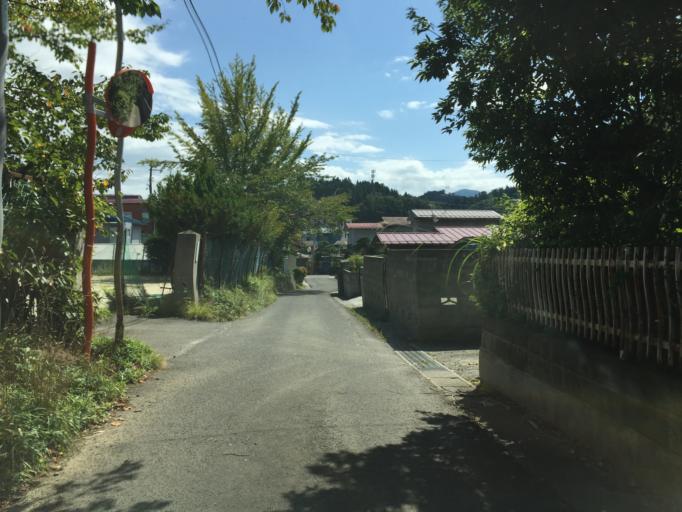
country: JP
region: Fukushima
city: Fukushima-shi
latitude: 37.6670
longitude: 140.5965
